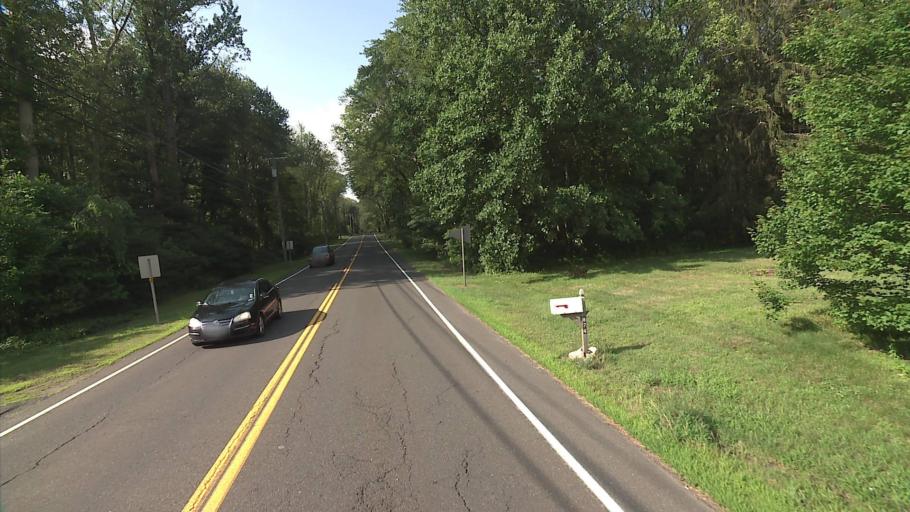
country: US
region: Connecticut
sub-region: Middlesex County
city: Higganum
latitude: 41.4385
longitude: -72.5568
